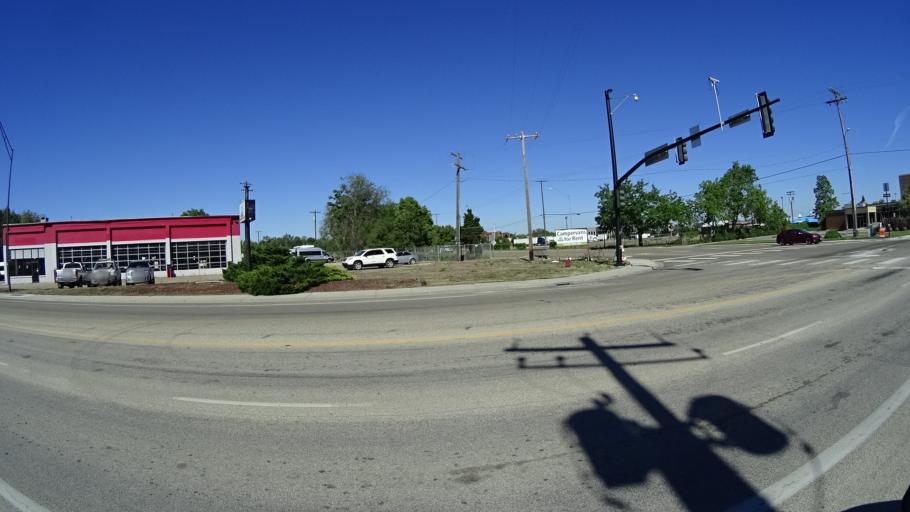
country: US
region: Idaho
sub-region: Ada County
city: Garden City
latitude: 43.6202
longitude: -116.2239
